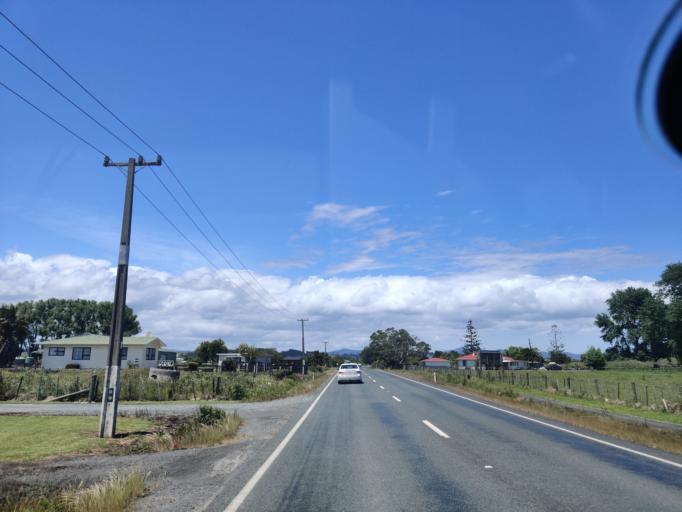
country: NZ
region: Northland
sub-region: Far North District
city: Kaitaia
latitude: -35.0409
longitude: 173.2558
